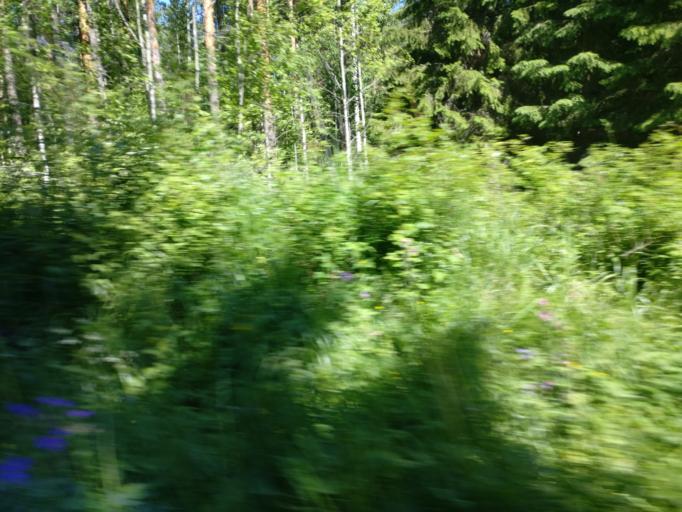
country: FI
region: Southern Savonia
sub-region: Savonlinna
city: Rantasalmi
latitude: 62.1556
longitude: 28.2418
